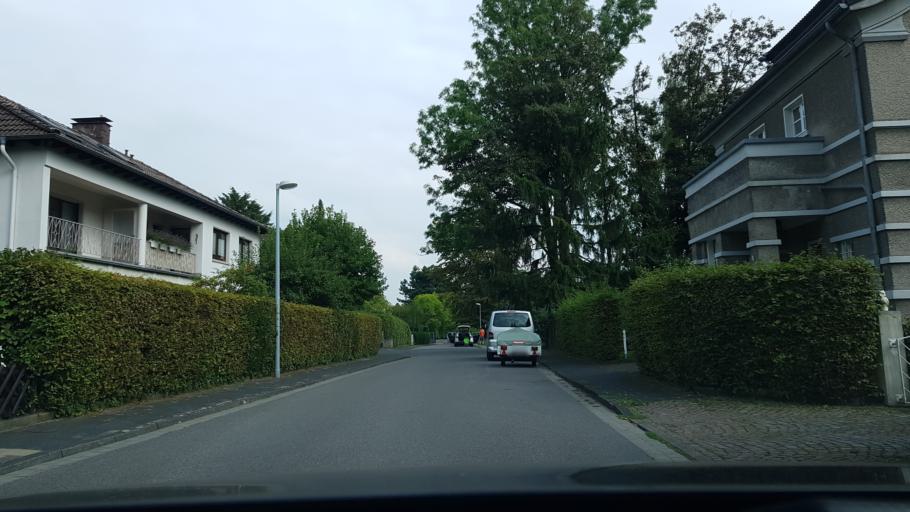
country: DE
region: North Rhine-Westphalia
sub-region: Regierungsbezirk Dusseldorf
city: Muelheim (Ruhr)
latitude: 51.4171
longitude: 6.8971
